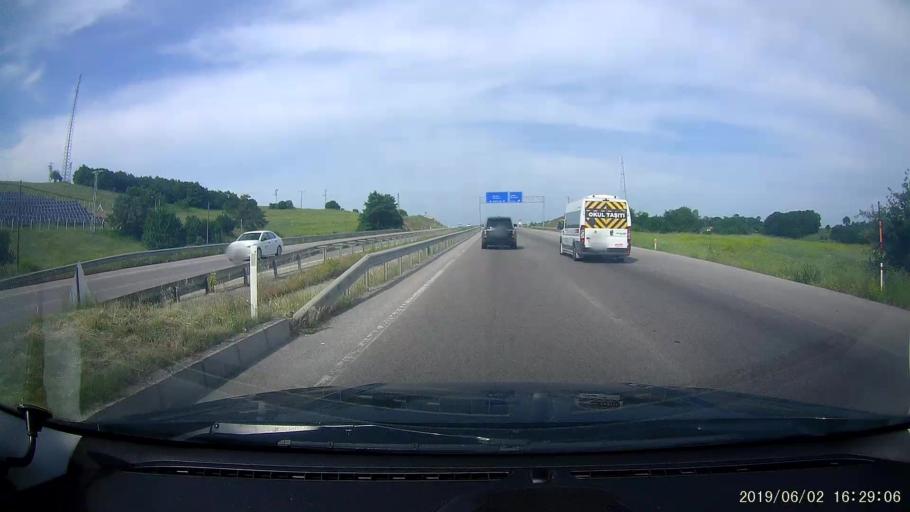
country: TR
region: Samsun
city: Ladik
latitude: 41.0108
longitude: 35.8622
